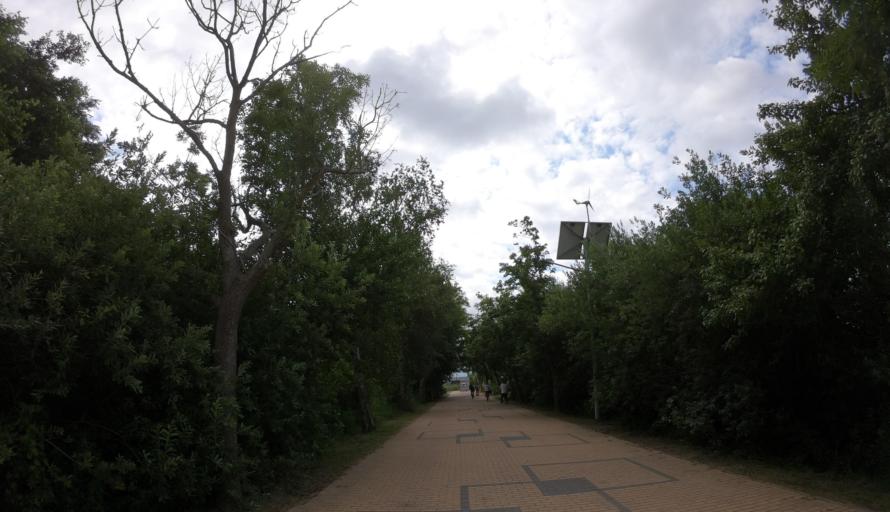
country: PL
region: West Pomeranian Voivodeship
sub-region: Powiat kamienski
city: Dziwnow
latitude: 54.0006
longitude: 14.7016
